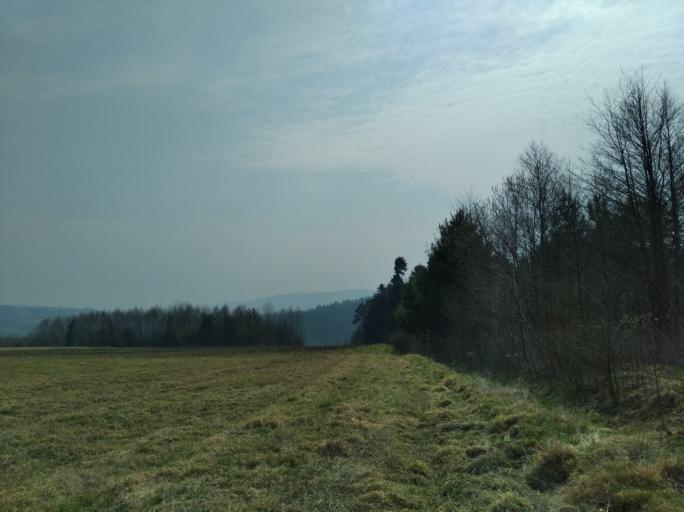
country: PL
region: Subcarpathian Voivodeship
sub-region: Powiat strzyzowski
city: Strzyzow
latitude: 49.8163
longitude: 21.8226
